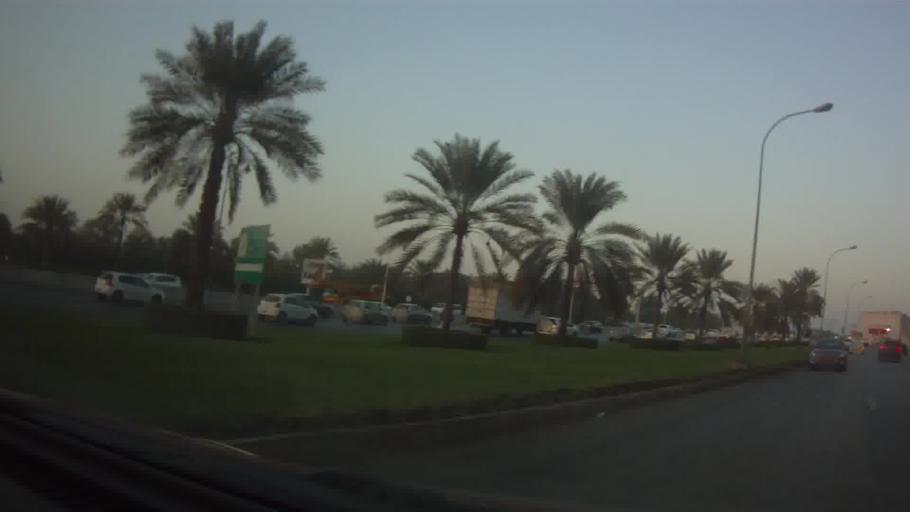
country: OM
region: Muhafazat Masqat
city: Bawshar
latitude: 23.5964
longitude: 58.4165
